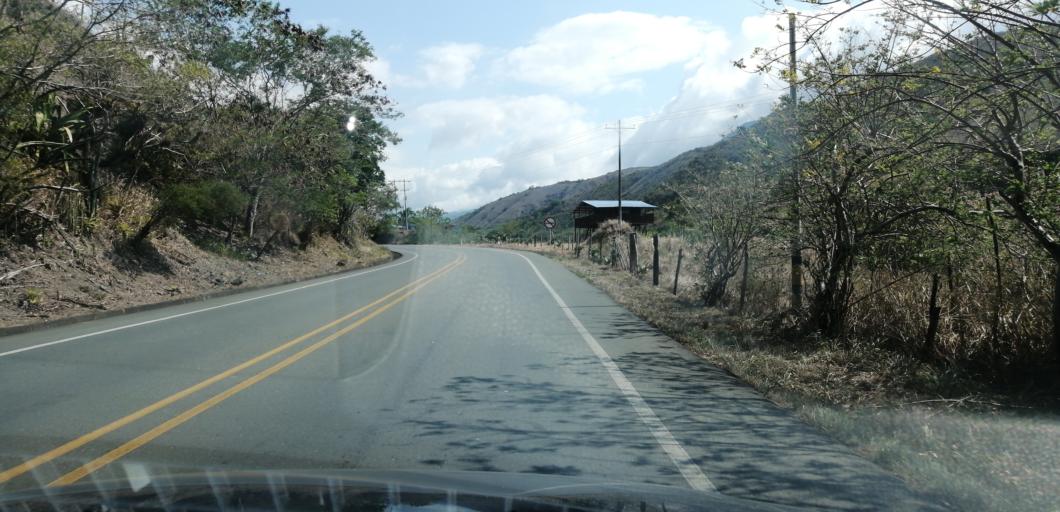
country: CO
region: Valle del Cauca
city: Dagua
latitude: 3.7409
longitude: -76.6638
